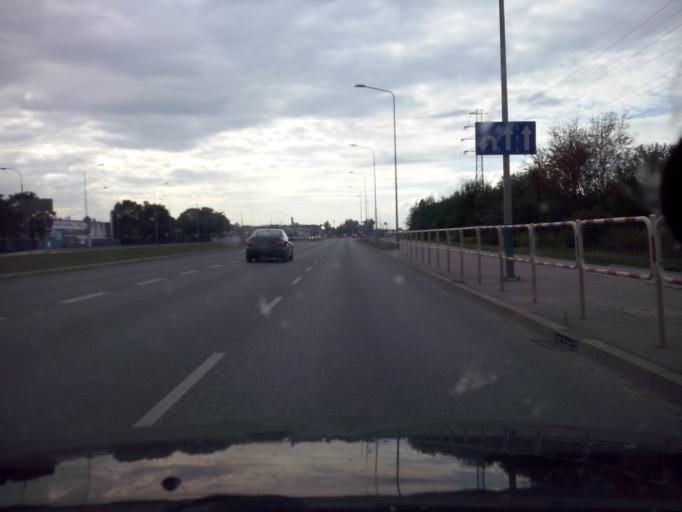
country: PL
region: Lesser Poland Voivodeship
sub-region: Powiat wielicki
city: Czarnochowice
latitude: 50.0378
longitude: 20.0228
